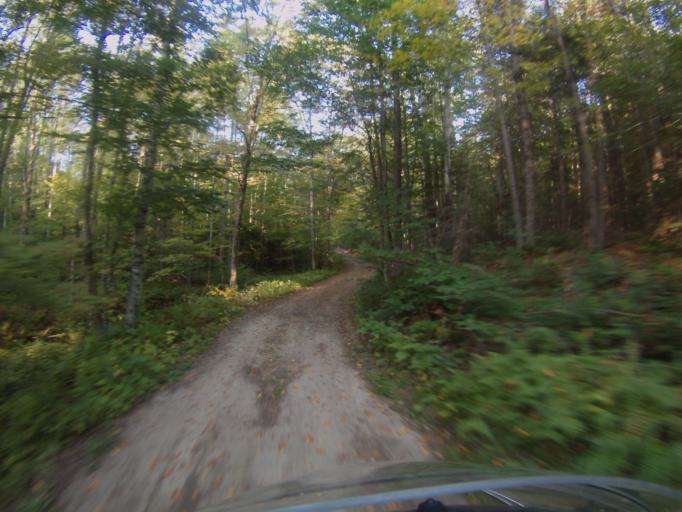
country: US
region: Vermont
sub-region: Addison County
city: Bristol
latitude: 44.0105
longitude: -73.0142
